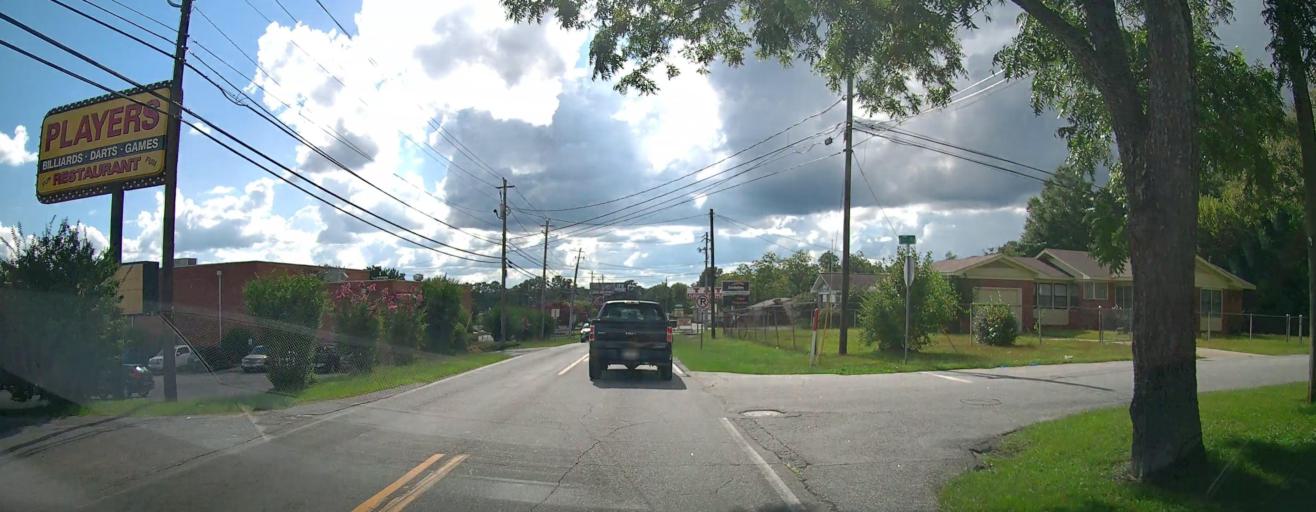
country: US
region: Alabama
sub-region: Russell County
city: Phenix City
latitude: 32.5207
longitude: -84.9656
